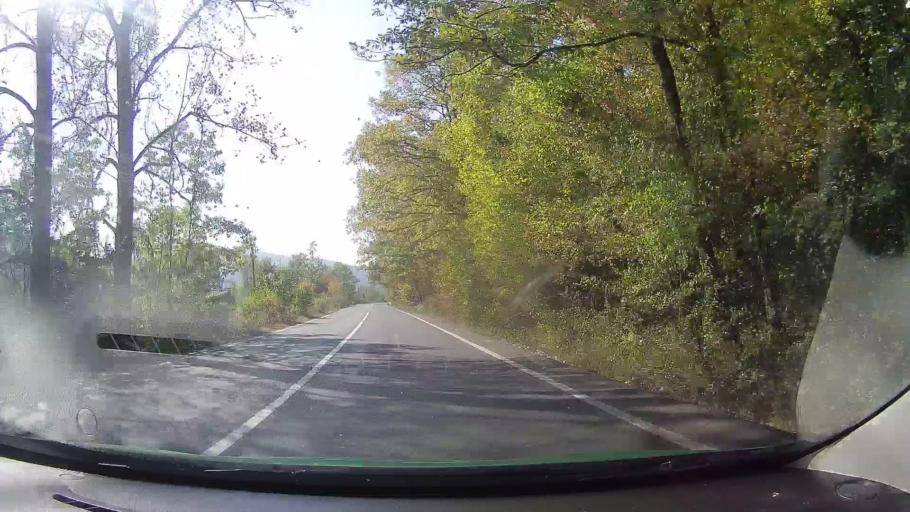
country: RO
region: Arad
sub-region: Comuna Petris
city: Petris
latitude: 46.0069
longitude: 22.3407
